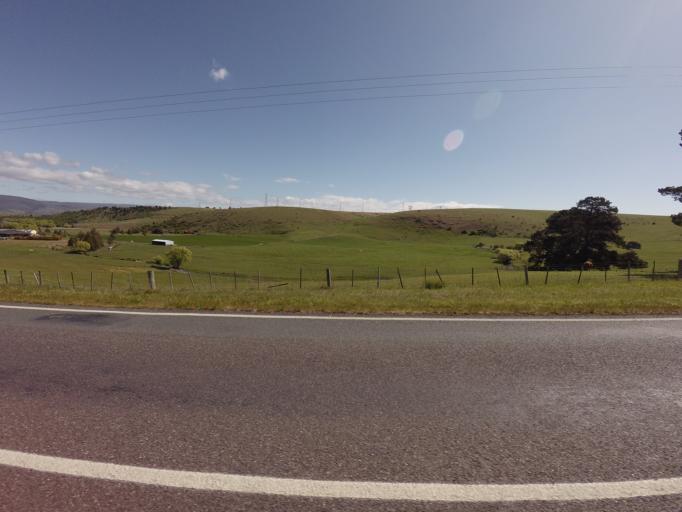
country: AU
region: Tasmania
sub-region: Derwent Valley
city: New Norfolk
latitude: -42.6572
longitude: 146.9355
